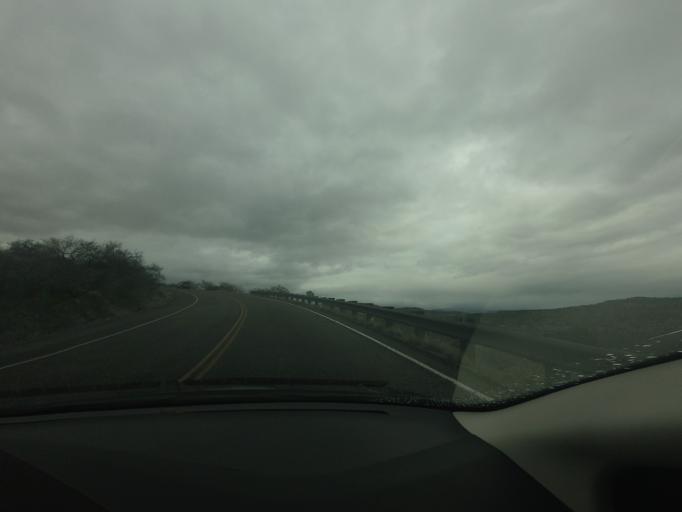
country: US
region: Arizona
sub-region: Yavapai County
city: Camp Verde
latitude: 34.6129
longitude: -111.8354
